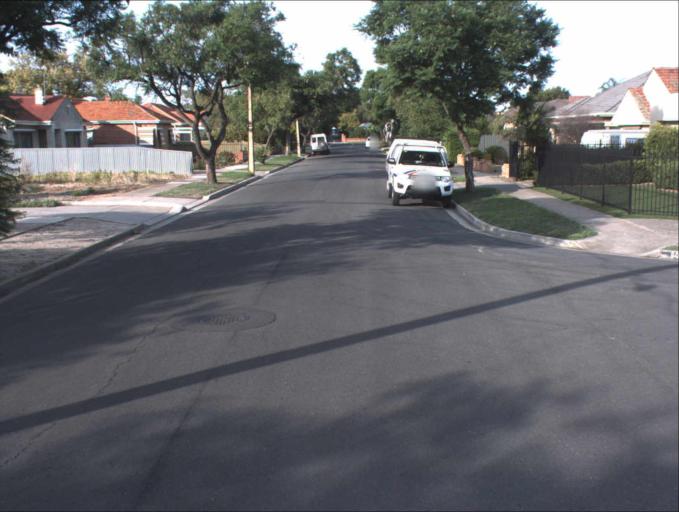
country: AU
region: South Australia
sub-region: Port Adelaide Enfield
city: Klemzig
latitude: -34.8773
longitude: 138.6273
